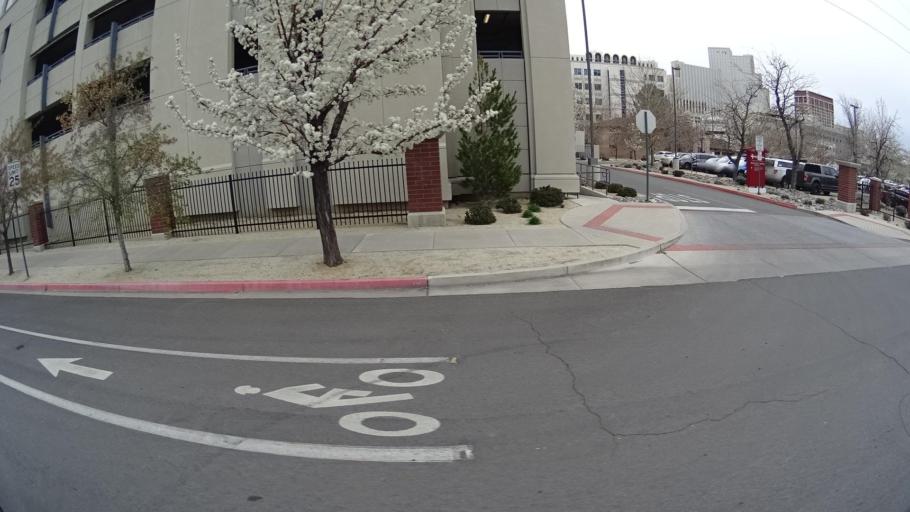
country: US
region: Nevada
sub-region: Washoe County
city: Reno
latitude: 39.5316
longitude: -119.8217
